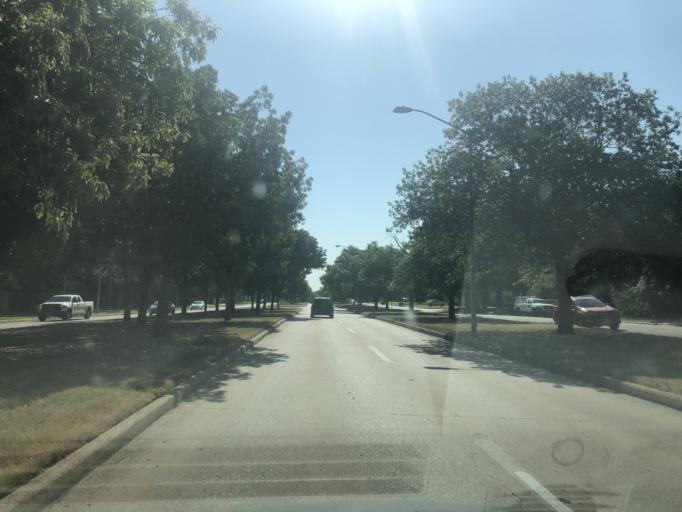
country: US
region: Texas
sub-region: Tarrant County
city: Edgecliff Village
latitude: 32.7018
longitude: -97.3735
